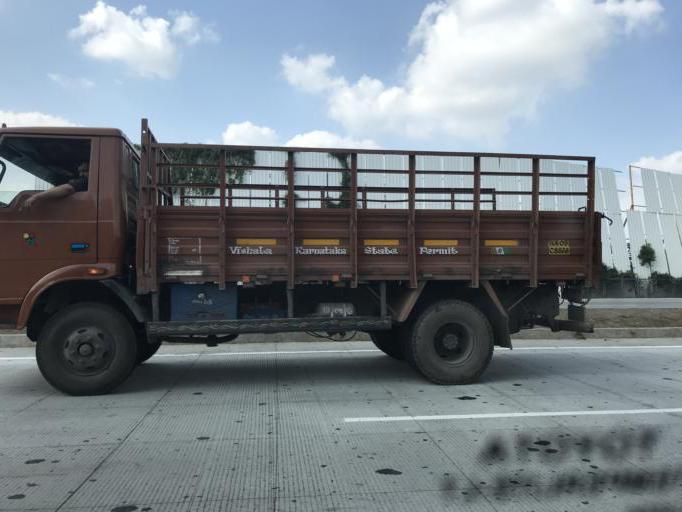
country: IN
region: Karnataka
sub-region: Bangalore Urban
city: Bangalore
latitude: 12.8809
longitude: 77.4974
